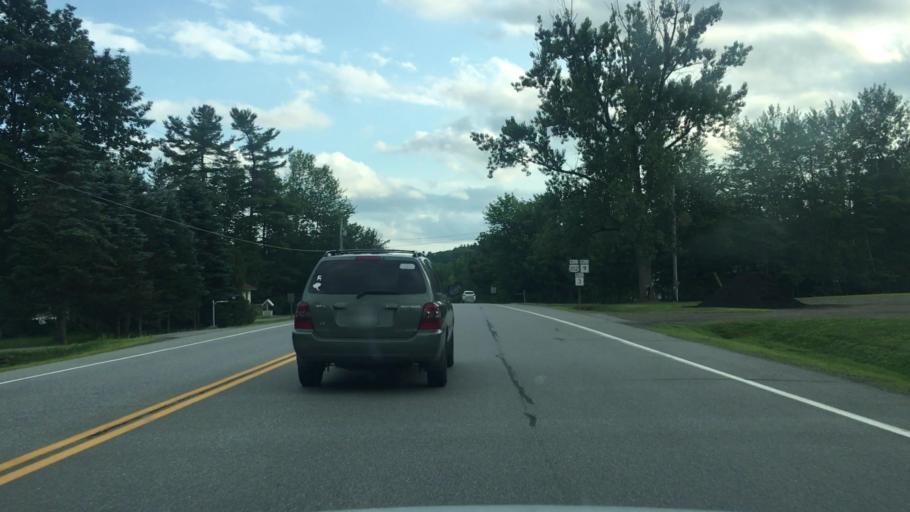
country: US
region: Maine
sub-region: Kennebec County
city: Windsor
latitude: 44.3753
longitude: -69.6258
